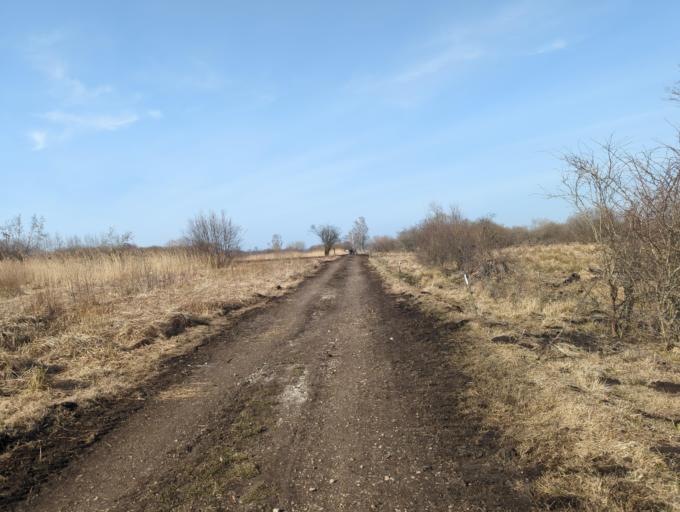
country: DE
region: Bavaria
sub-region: Swabia
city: Leipheim
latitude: 48.4795
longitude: 10.2148
